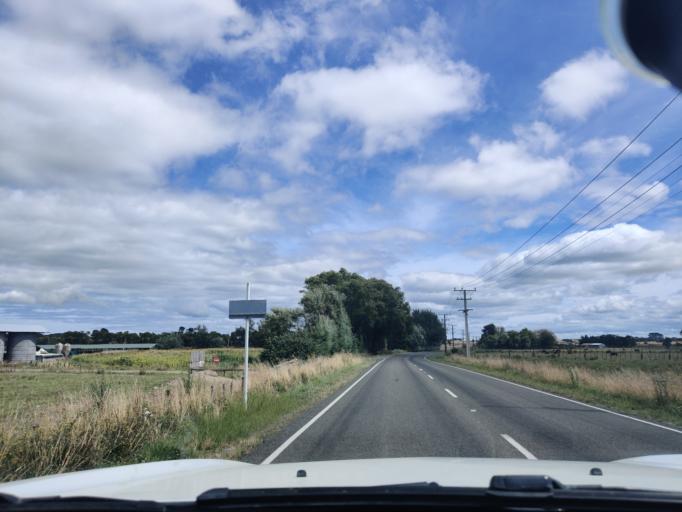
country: NZ
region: Manawatu-Wanganui
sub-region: Horowhenua District
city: Foxton
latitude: -40.4913
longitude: 175.3658
